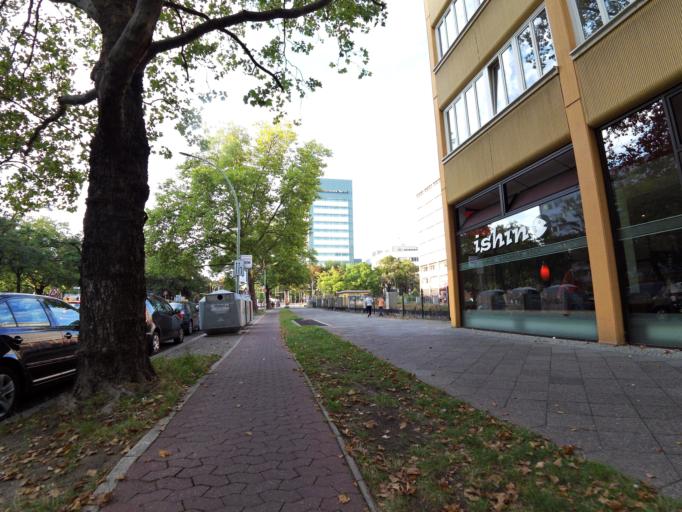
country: DE
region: Berlin
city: Wilmersdorf Bezirk
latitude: 52.4942
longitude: 13.3311
